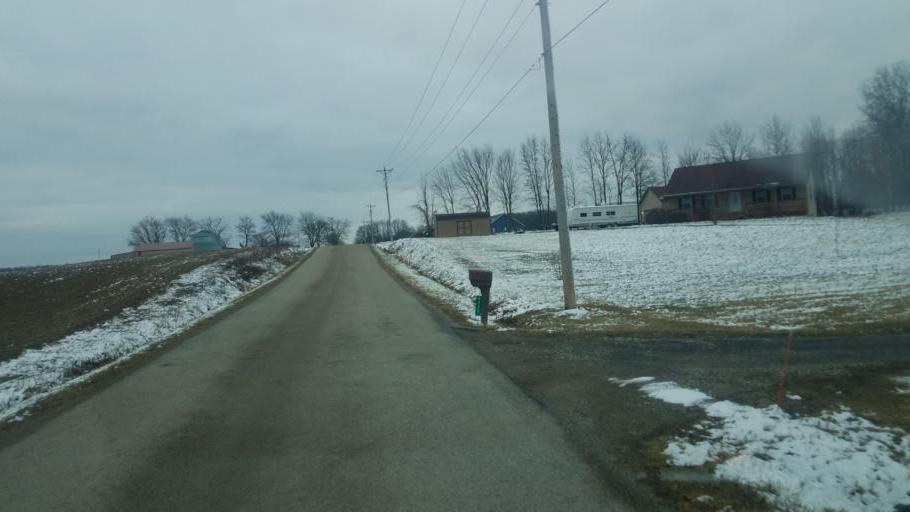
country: US
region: Ohio
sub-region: Morrow County
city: Mount Gilead
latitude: 40.4757
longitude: -82.7748
